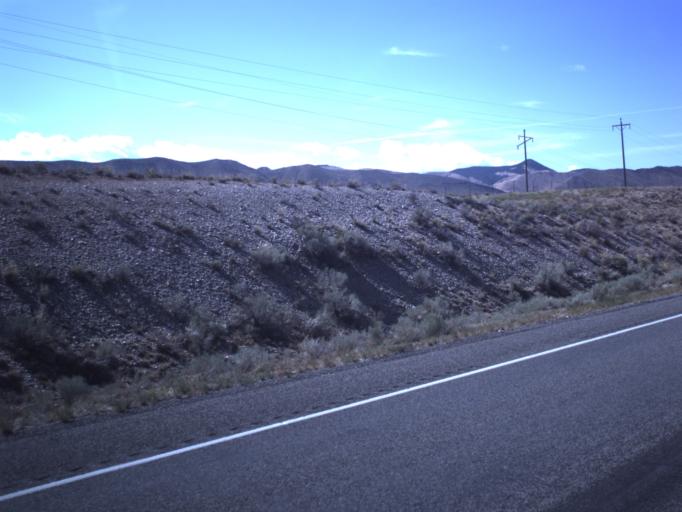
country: US
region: Utah
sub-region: Sevier County
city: Salina
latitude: 39.0166
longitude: -111.8345
